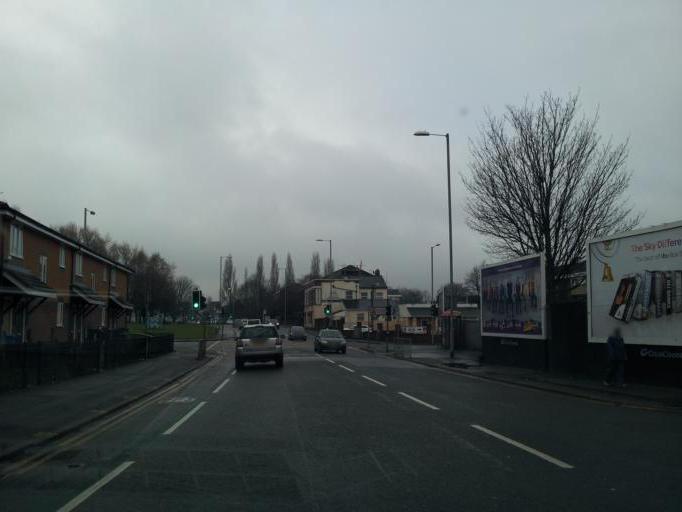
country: GB
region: England
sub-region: Manchester
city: Blackley
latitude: 53.5087
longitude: -2.2170
